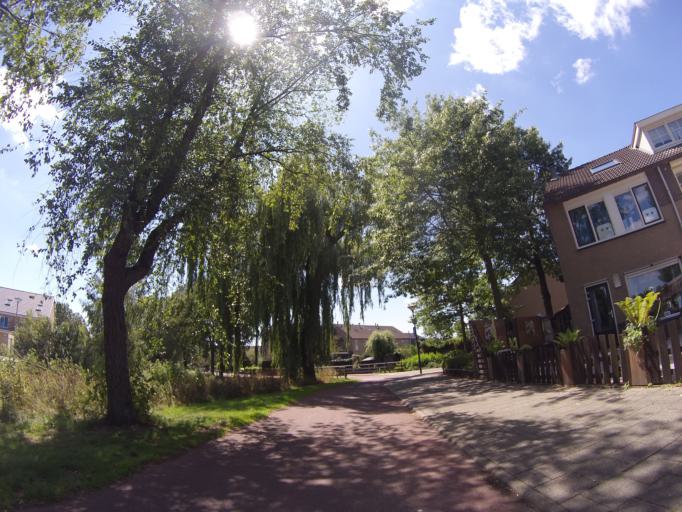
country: NL
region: Utrecht
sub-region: Stichtse Vecht
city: Spechtenkamp
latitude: 52.1387
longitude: 5.0205
